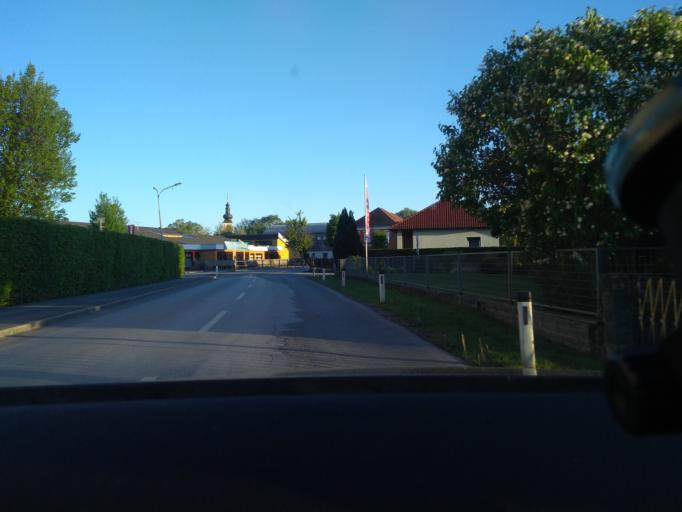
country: AT
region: Styria
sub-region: Politischer Bezirk Voitsberg
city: Mooskirchen
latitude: 46.9876
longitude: 15.2815
